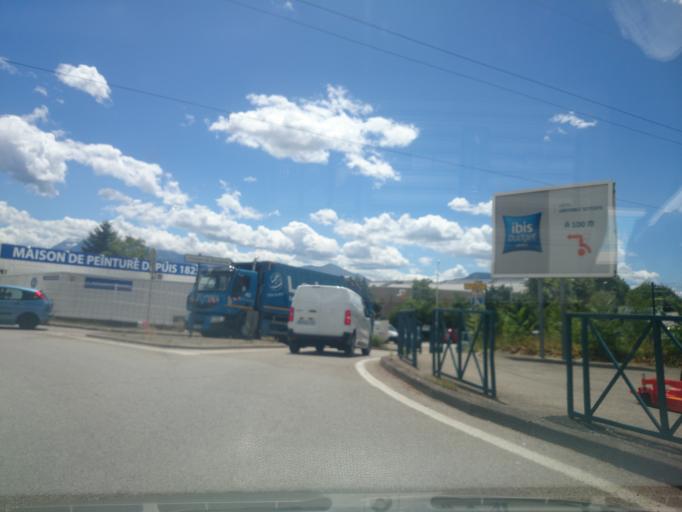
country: FR
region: Rhone-Alpes
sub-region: Departement de l'Isere
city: Seyssins
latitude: 45.1593
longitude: 5.6958
